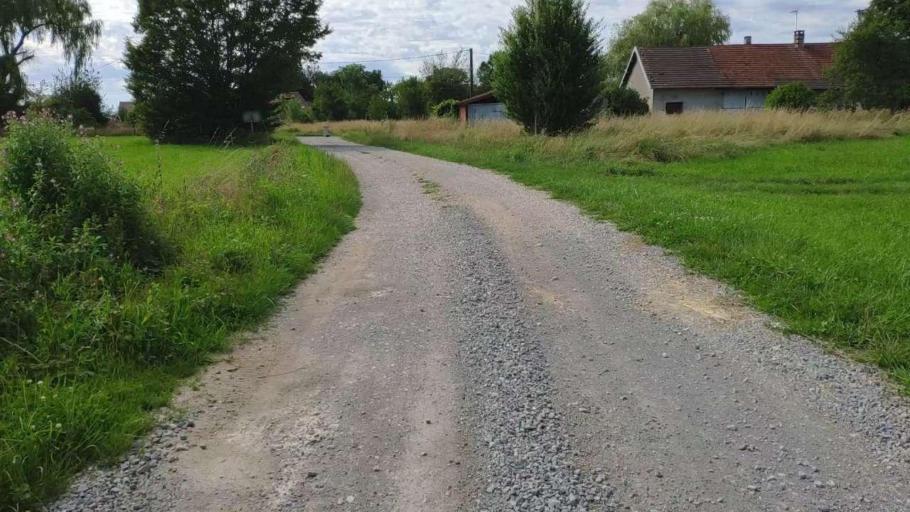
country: FR
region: Franche-Comte
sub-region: Departement du Jura
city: Bletterans
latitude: 46.8030
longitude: 5.4569
